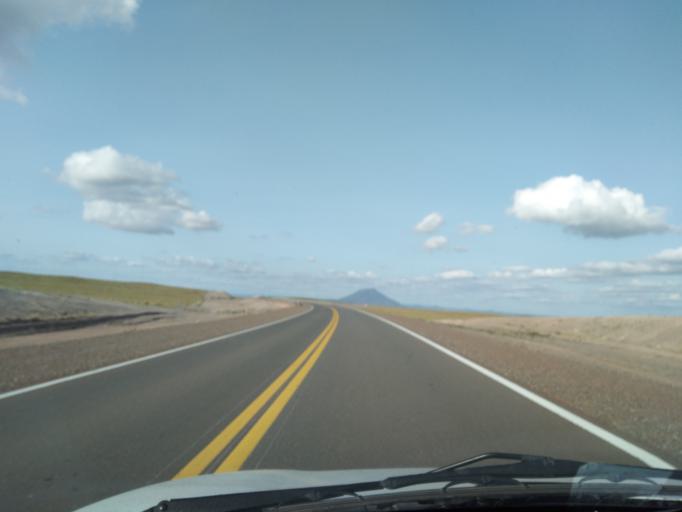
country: AR
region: Mendoza
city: Malargue
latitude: -34.8183
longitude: -69.2494
